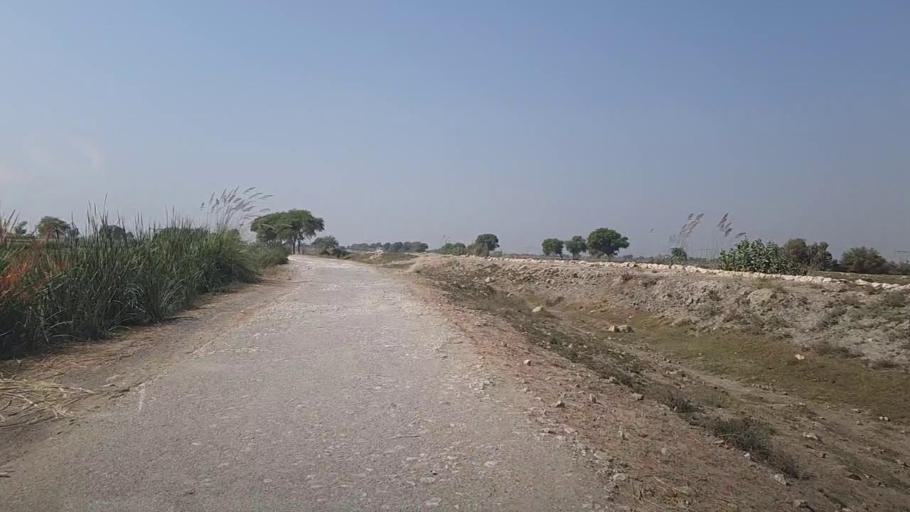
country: PK
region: Sindh
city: Kandhkot
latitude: 28.3901
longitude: 69.3354
